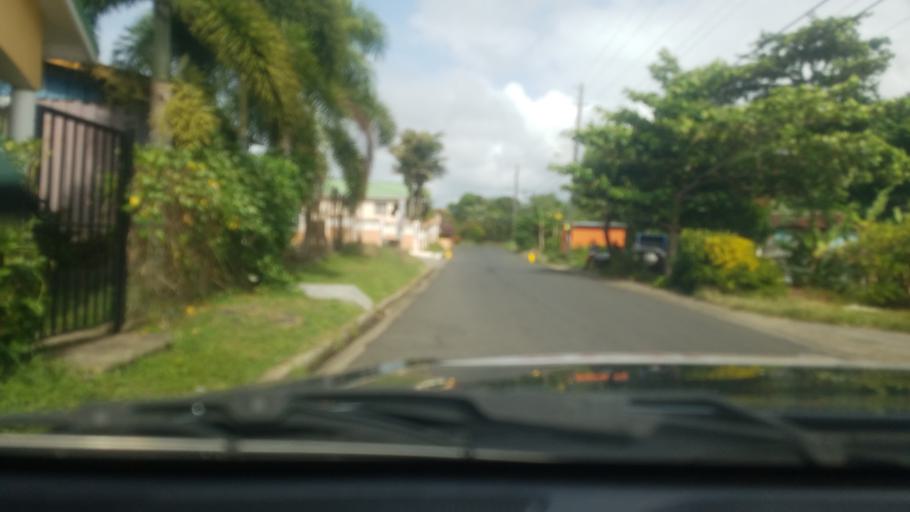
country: LC
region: Micoud Quarter
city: Micoud
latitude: 13.7984
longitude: -60.9199
